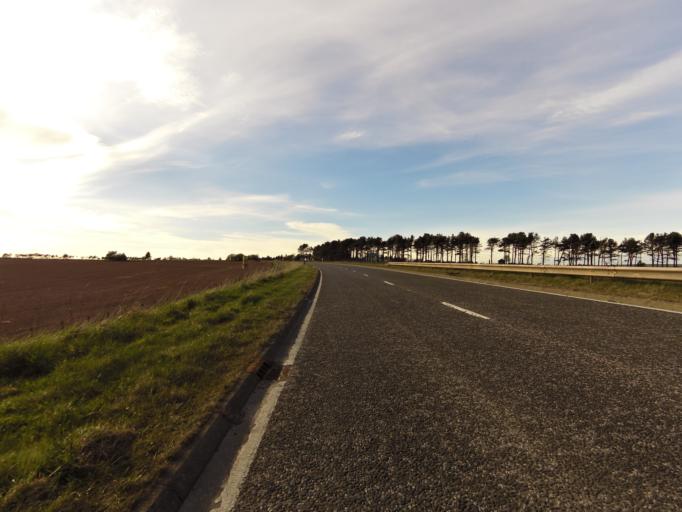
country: GB
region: Scotland
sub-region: Aberdeenshire
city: Stonehaven
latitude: 56.9437
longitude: -2.2095
